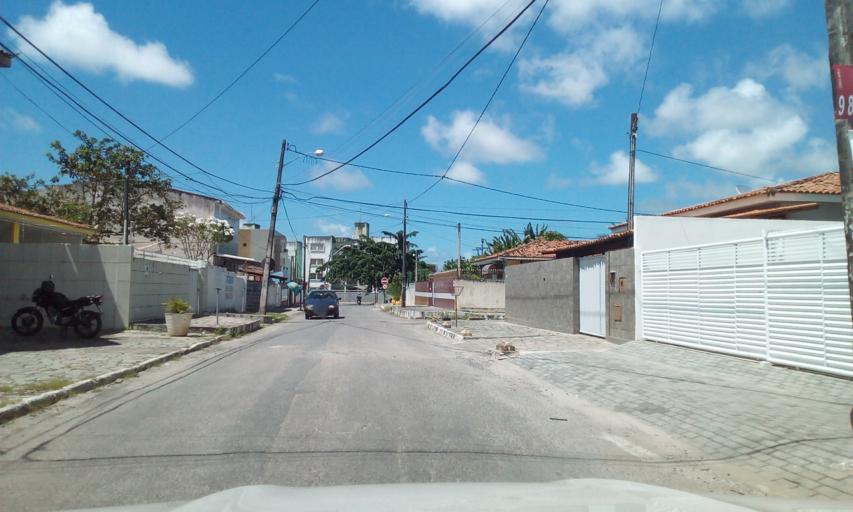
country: BR
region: Paraiba
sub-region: Joao Pessoa
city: Joao Pessoa
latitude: -7.1712
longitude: -34.8605
